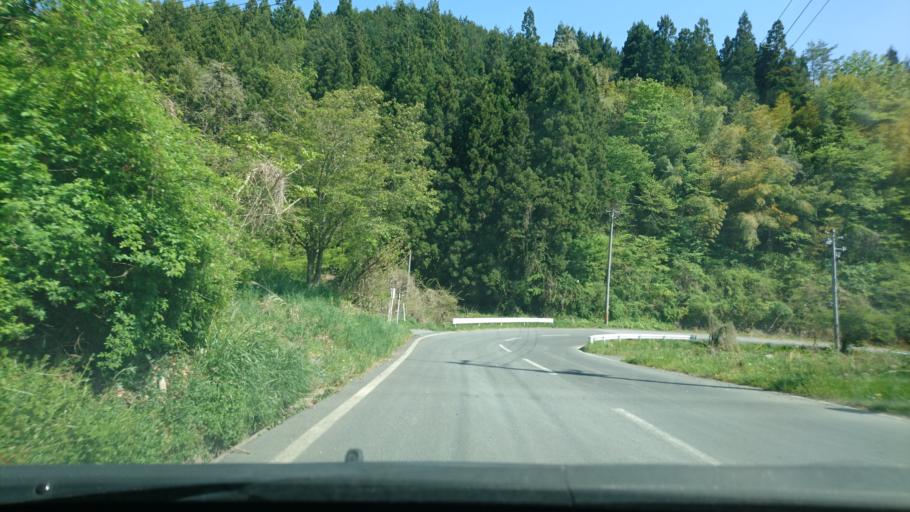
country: JP
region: Iwate
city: Ichinoseki
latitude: 38.9352
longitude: 141.2795
